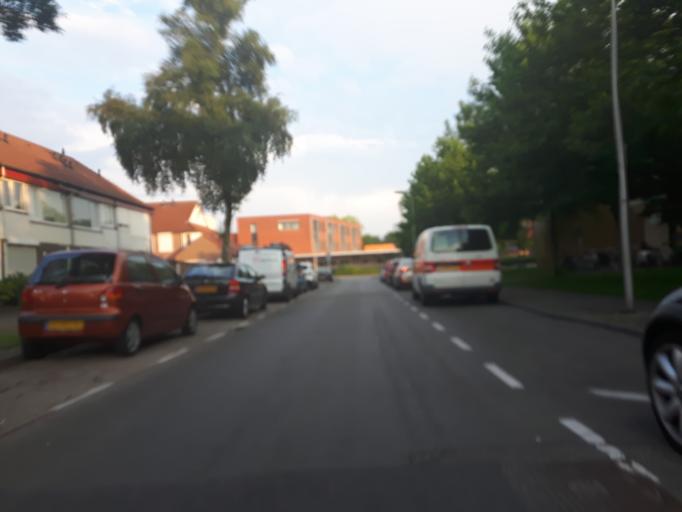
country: NL
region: Overijssel
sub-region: Gemeente Enschede
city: Enschede
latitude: 52.2123
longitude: 6.8584
